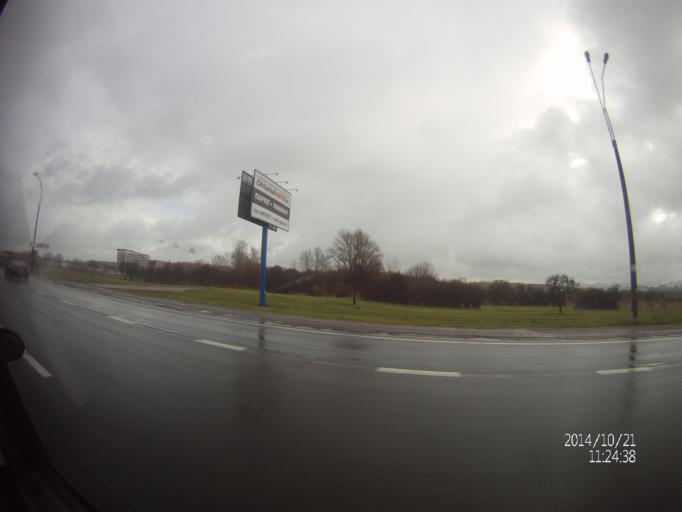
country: BY
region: Minsk
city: Zhdanovichy
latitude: 53.9476
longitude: 27.4414
